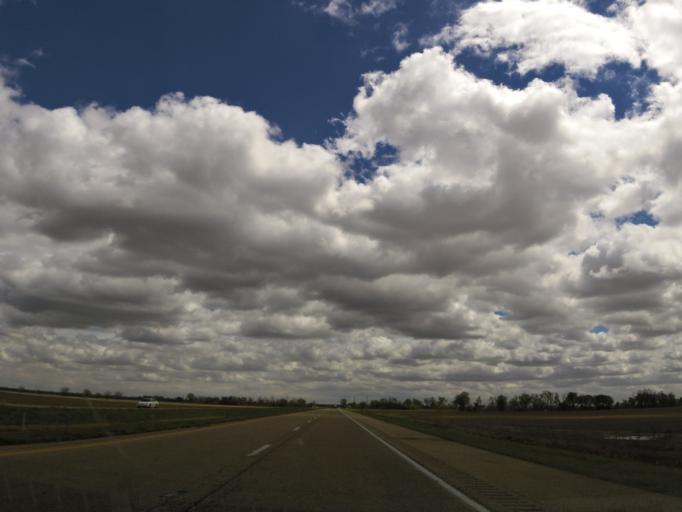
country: US
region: Arkansas
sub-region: Poinsett County
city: Trumann
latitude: 35.6524
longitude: -90.5311
